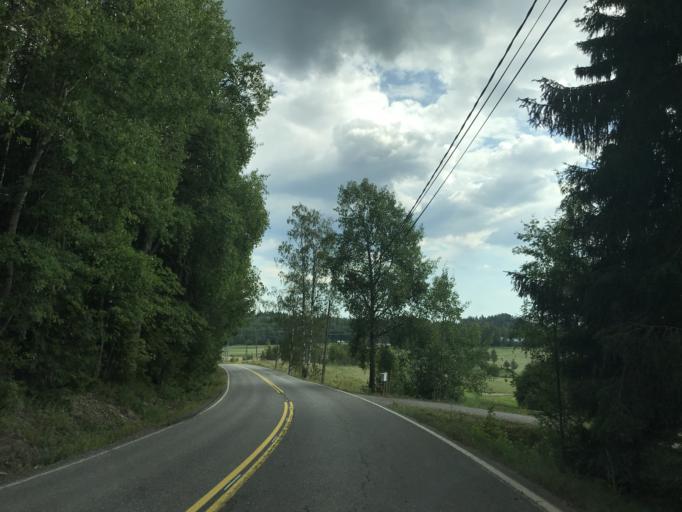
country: FI
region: Uusimaa
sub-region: Helsinki
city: Vihti
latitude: 60.3833
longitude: 24.3516
